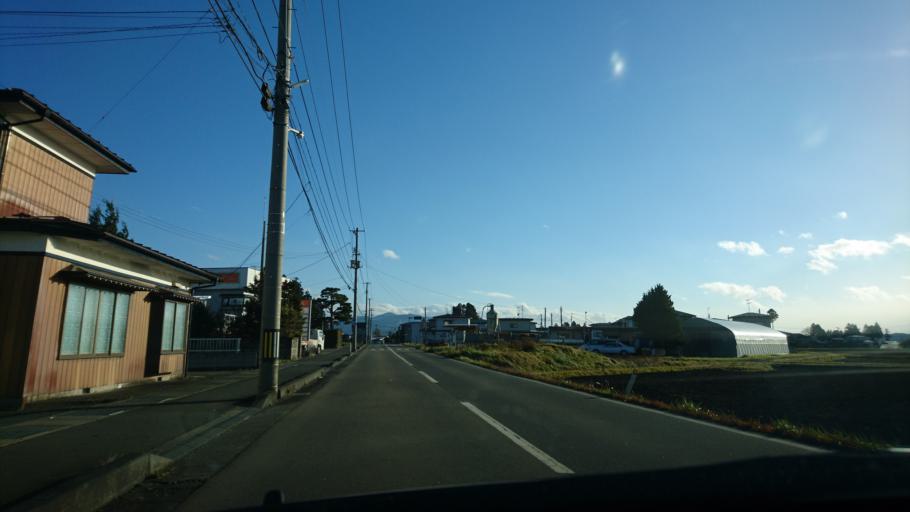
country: JP
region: Iwate
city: Mizusawa
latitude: 39.1120
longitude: 141.1553
